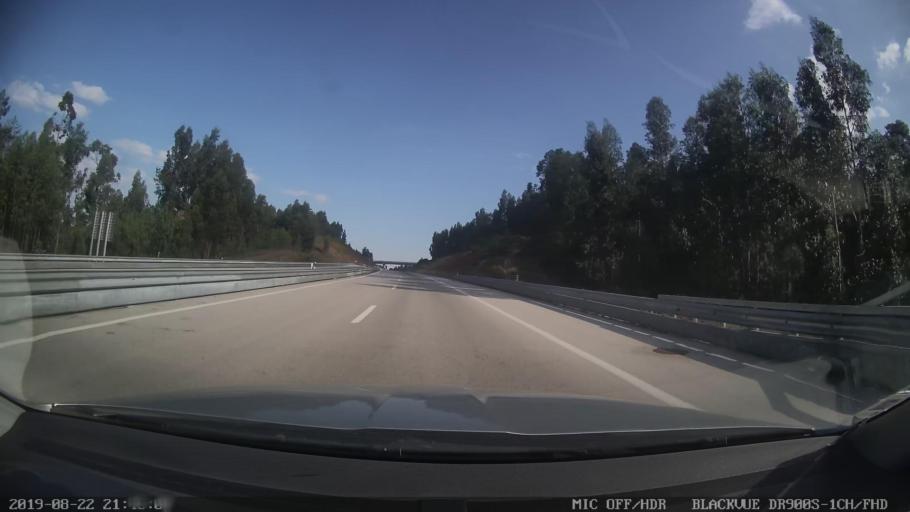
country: PT
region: Coimbra
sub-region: Penela
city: Penela
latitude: 39.9618
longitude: -8.3503
